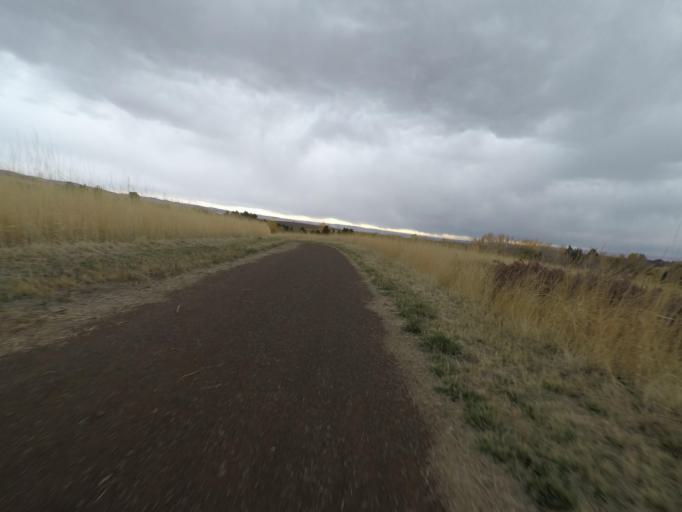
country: US
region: Washington
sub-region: Walla Walla County
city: Walla Walla East
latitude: 46.0694
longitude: -118.2568
